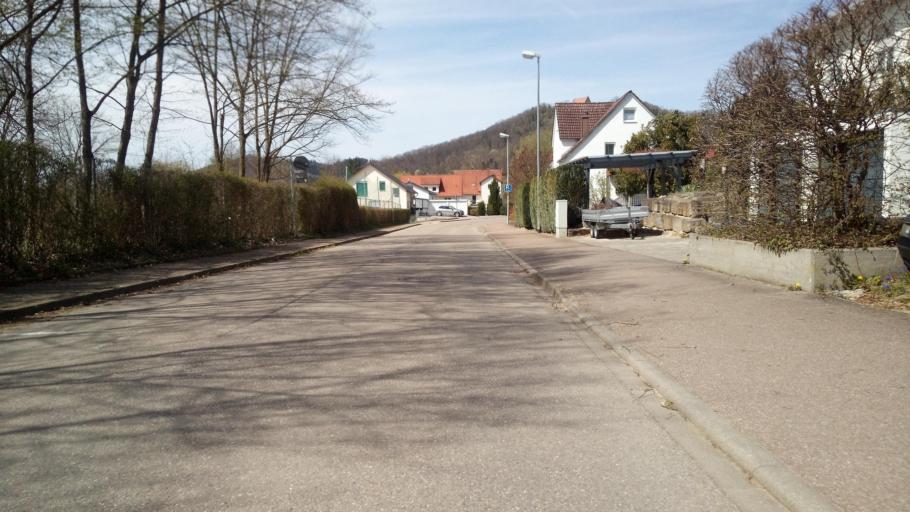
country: DE
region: Baden-Wuerttemberg
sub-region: Regierungsbezirk Stuttgart
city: Donzdorf
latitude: 48.6885
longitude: 9.7987
